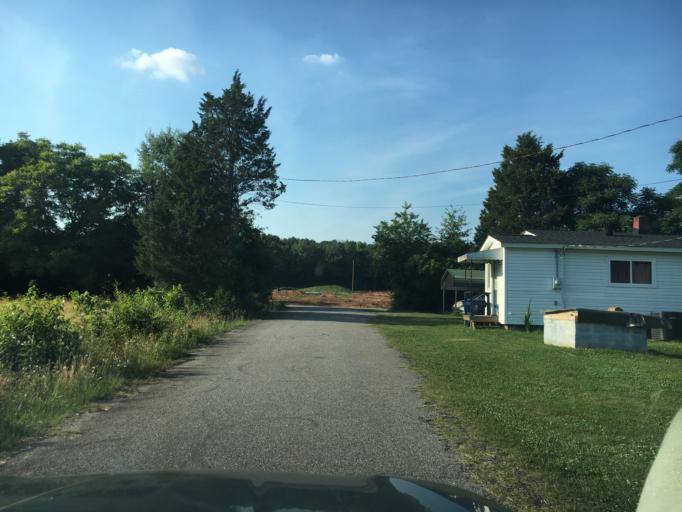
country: US
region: South Carolina
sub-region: Spartanburg County
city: Duncan
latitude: 34.8600
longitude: -82.1089
